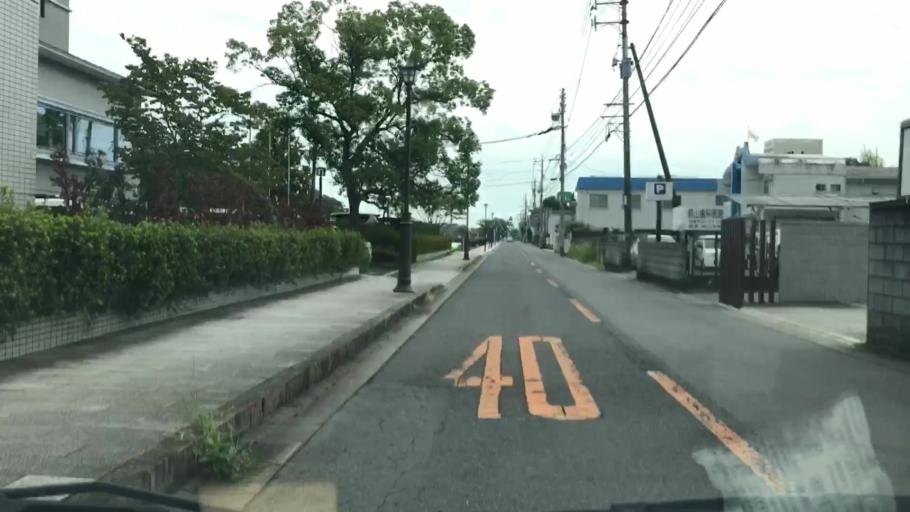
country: JP
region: Saga Prefecture
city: Saga-shi
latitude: 33.2497
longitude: 130.2954
